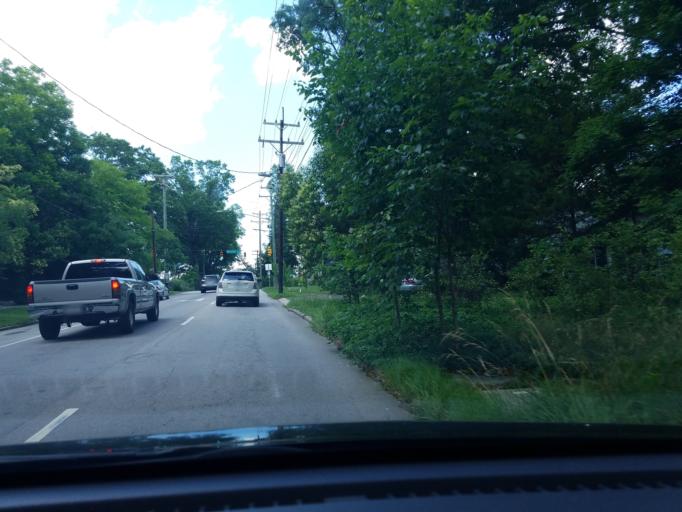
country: US
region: North Carolina
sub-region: Durham County
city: Durham
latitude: 36.0092
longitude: -78.9056
